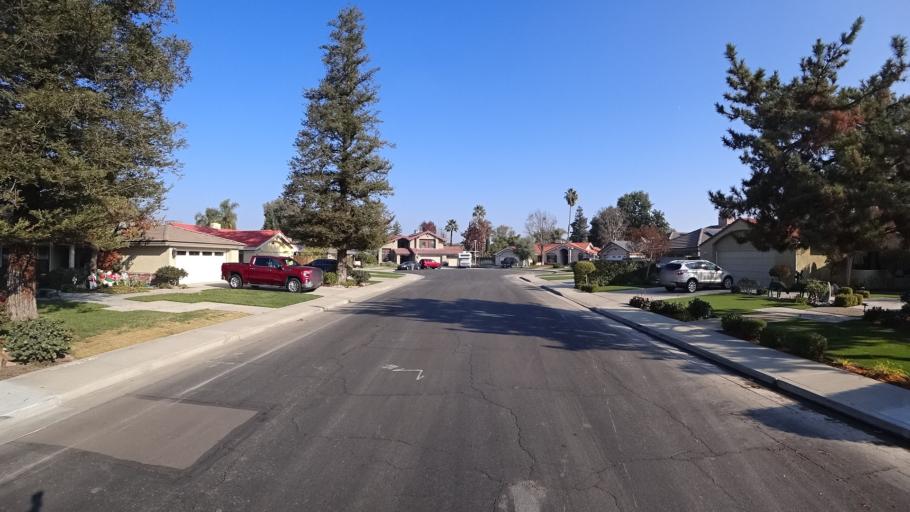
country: US
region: California
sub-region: Kern County
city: Greenacres
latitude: 35.3374
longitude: -119.1108
